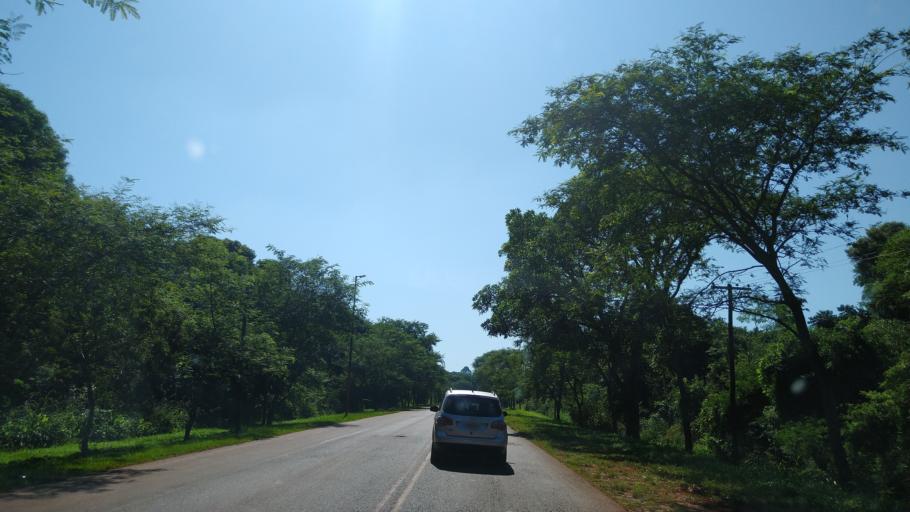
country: AR
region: Misiones
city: Puerto Esperanza
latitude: -26.0203
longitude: -54.5955
